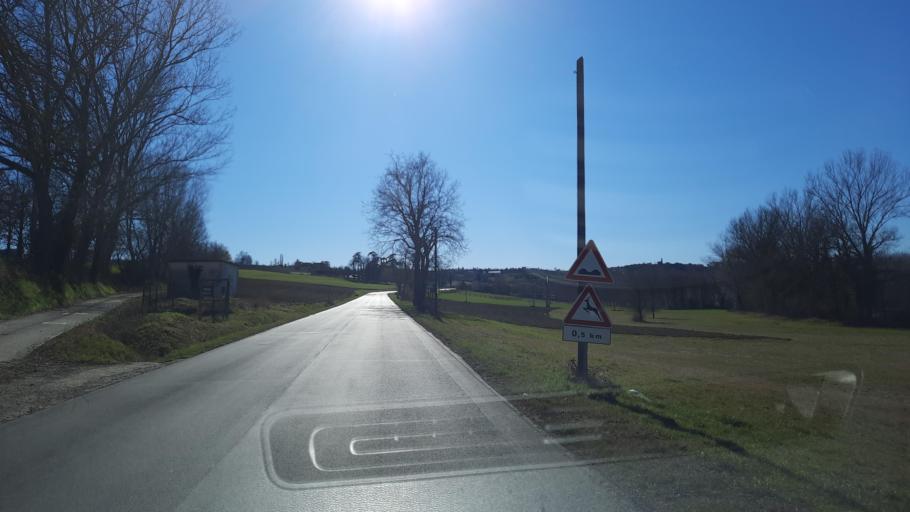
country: IT
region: Piedmont
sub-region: Provincia di Alessandria
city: Frassinello Monferrato
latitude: 45.0476
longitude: 8.3919
